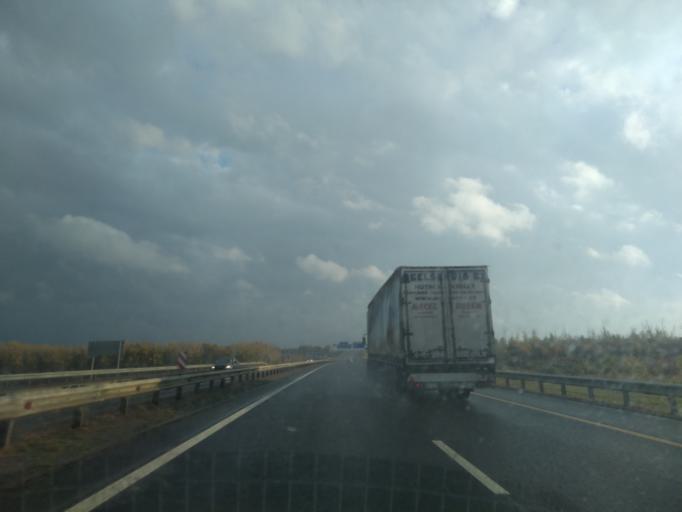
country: RU
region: Lipetsk
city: Yelets
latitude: 52.5557
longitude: 38.7154
